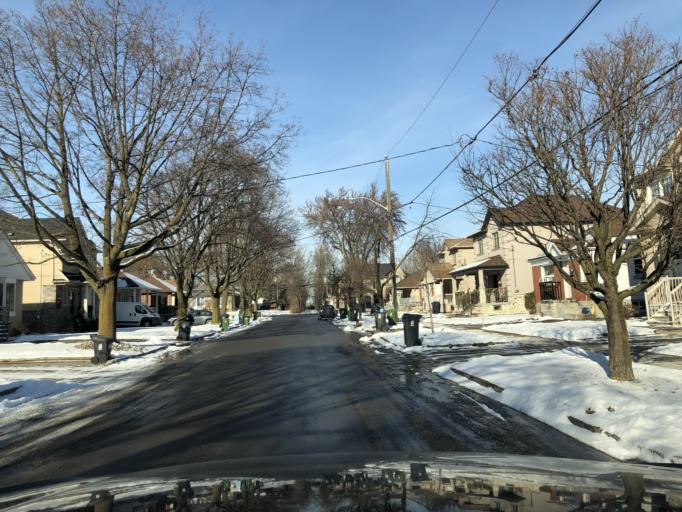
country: CA
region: Ontario
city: Etobicoke
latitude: 43.7098
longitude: -79.5203
